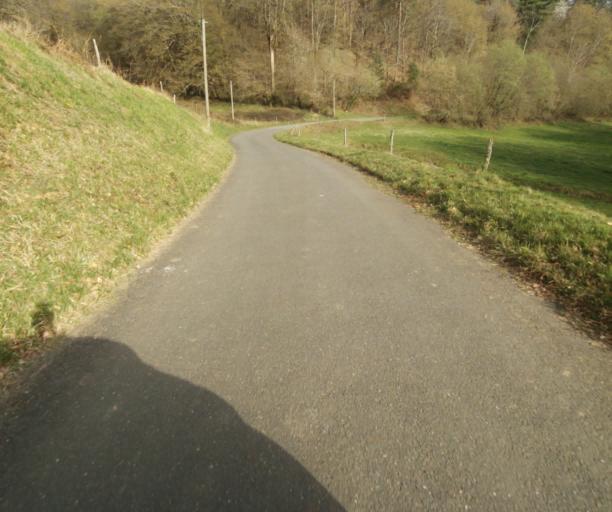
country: FR
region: Limousin
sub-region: Departement de la Correze
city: Naves
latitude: 45.2951
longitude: 1.7574
